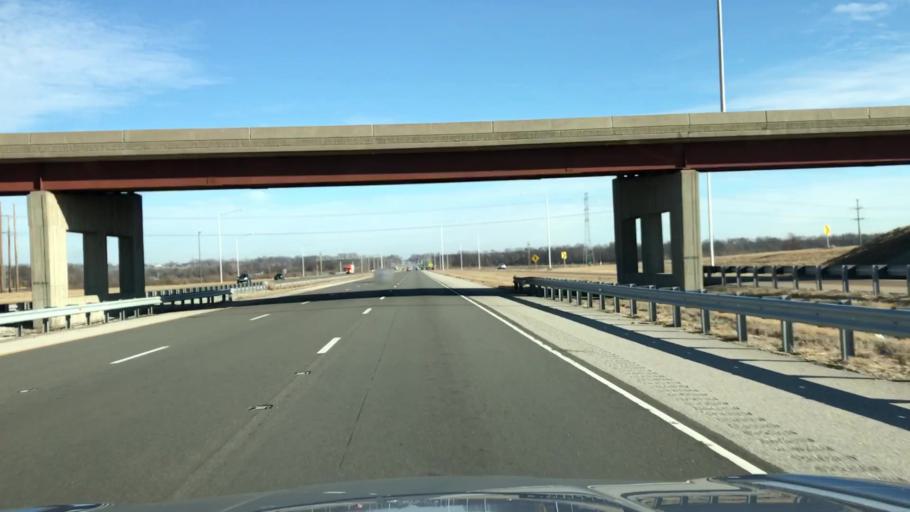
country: US
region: Illinois
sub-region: Madison County
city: Mitchell
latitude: 38.7570
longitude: -90.0408
